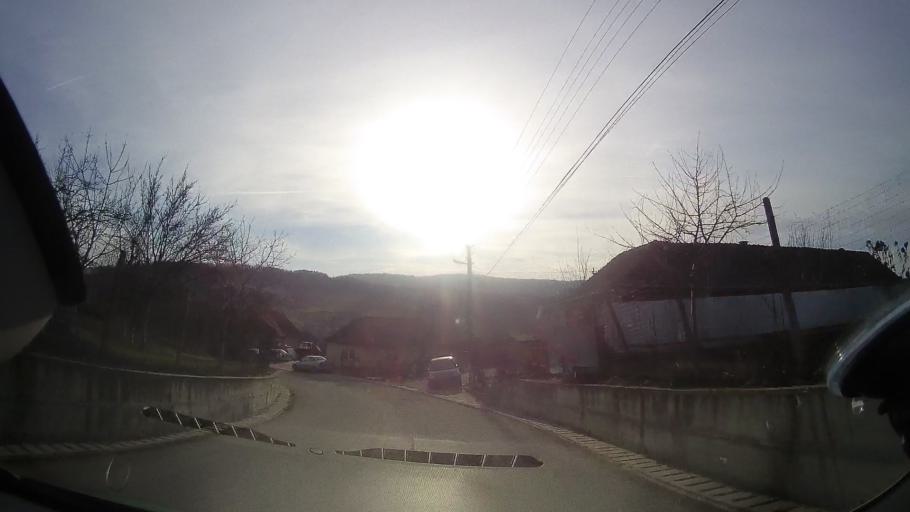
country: RO
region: Bihor
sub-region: Comuna Sarbi
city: Burzuc
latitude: 47.1495
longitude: 22.1751
